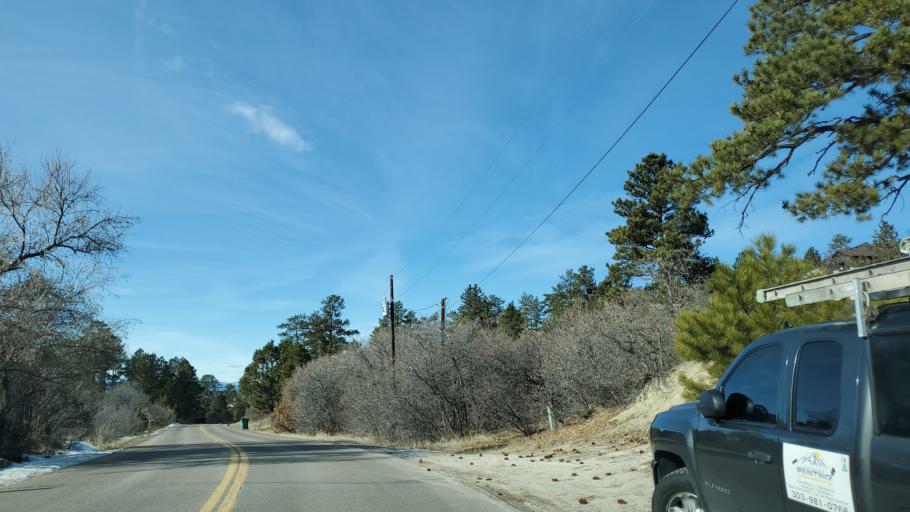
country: US
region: Colorado
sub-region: Douglas County
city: Castle Pines
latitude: 39.4349
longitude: -104.8700
